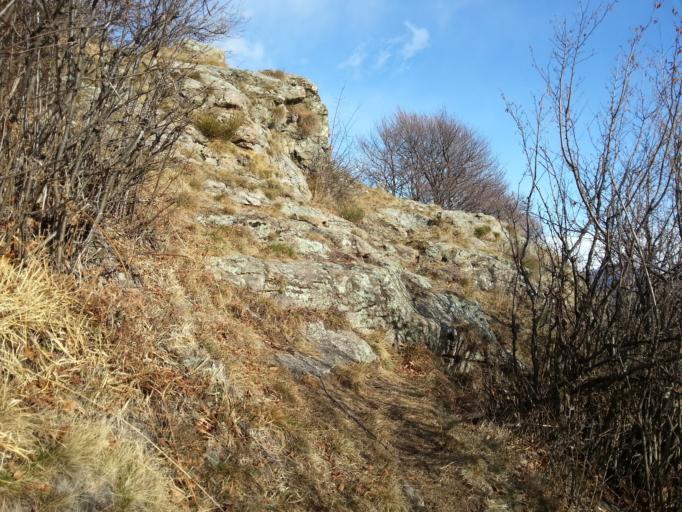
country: CH
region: Ticino
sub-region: Lugano District
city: Gravesano
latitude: 46.0465
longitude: 8.8693
